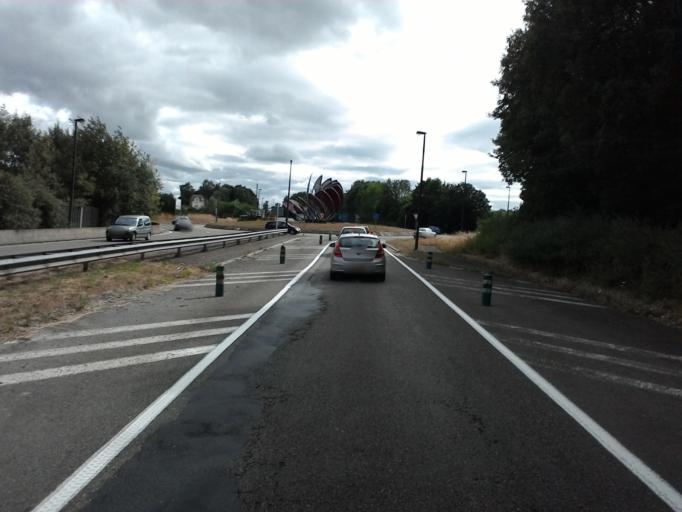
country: BE
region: Wallonia
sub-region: Province du Luxembourg
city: Arlon
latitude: 49.6899
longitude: 5.7922
